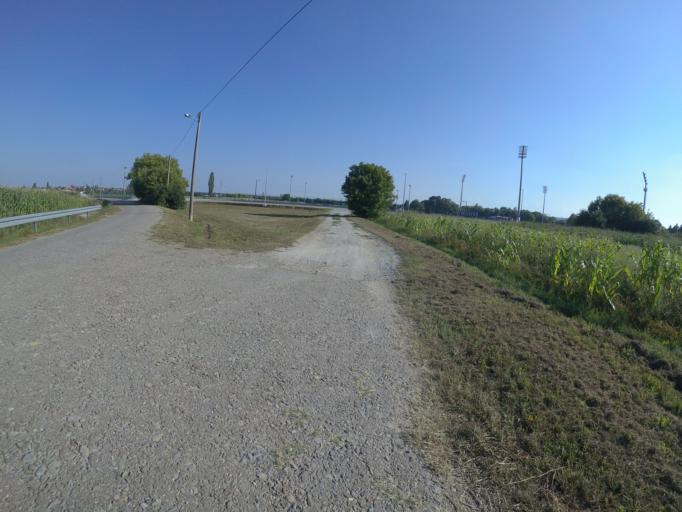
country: HR
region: Karlovacka
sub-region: Grad Karlovac
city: Karlovac
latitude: 45.4869
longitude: 15.5655
